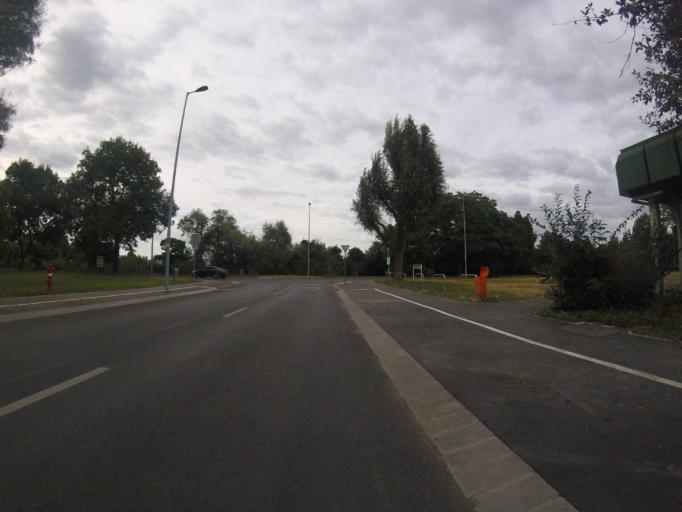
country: HU
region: Pest
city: Budakalasz
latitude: 47.6036
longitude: 19.0658
